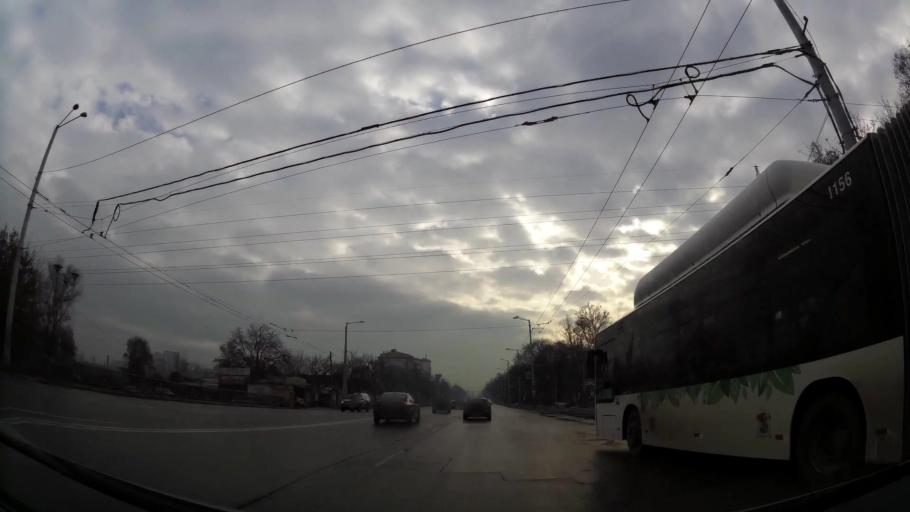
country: BG
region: Sofia-Capital
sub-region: Stolichna Obshtina
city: Sofia
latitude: 42.7171
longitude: 23.2796
